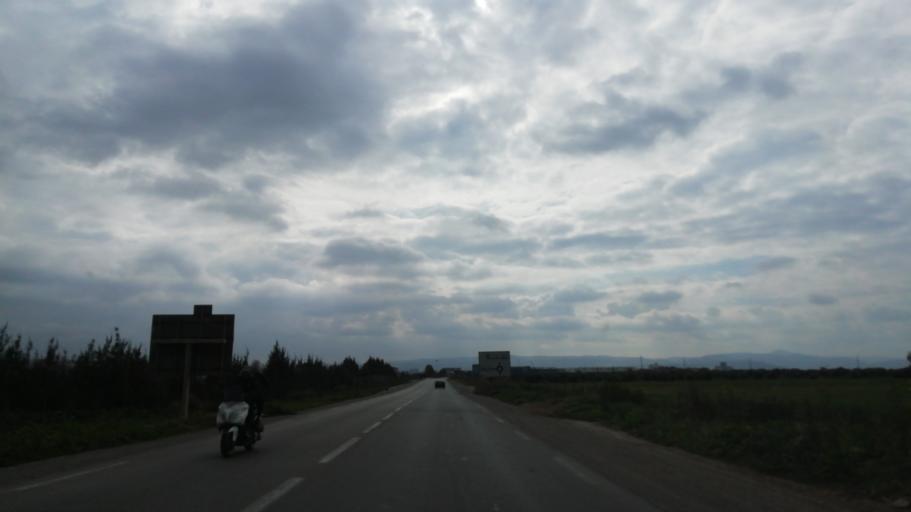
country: DZ
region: Oran
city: Sidi ech Chahmi
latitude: 35.5703
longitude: -0.4504
